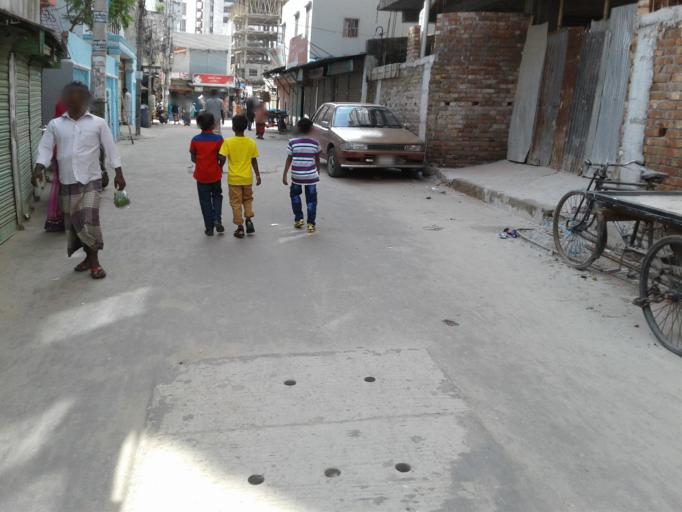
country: BD
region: Dhaka
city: Azimpur
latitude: 23.8095
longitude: 90.3788
